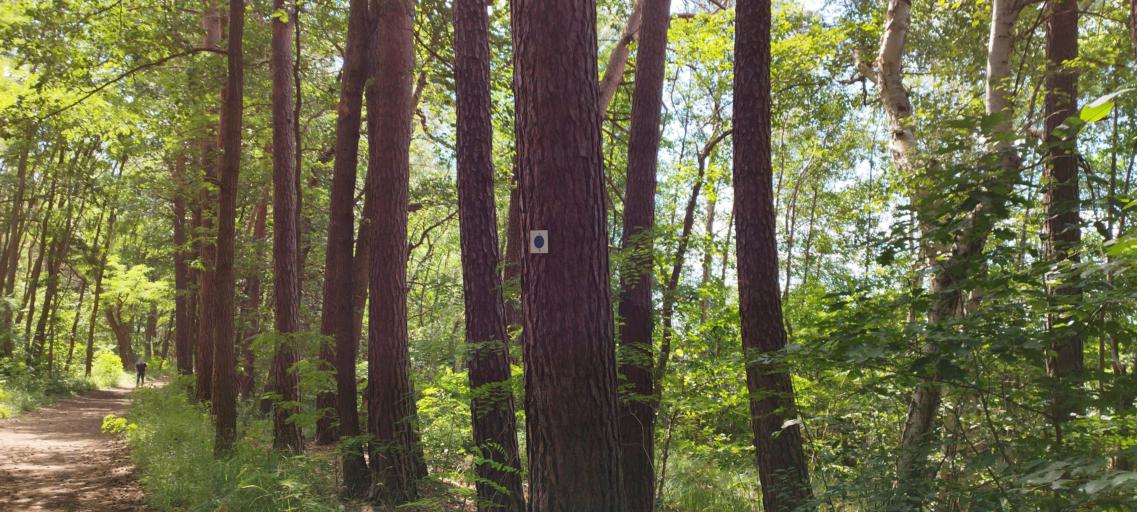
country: DE
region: Brandenburg
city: Reichenwalde
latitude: 52.2980
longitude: 13.9990
